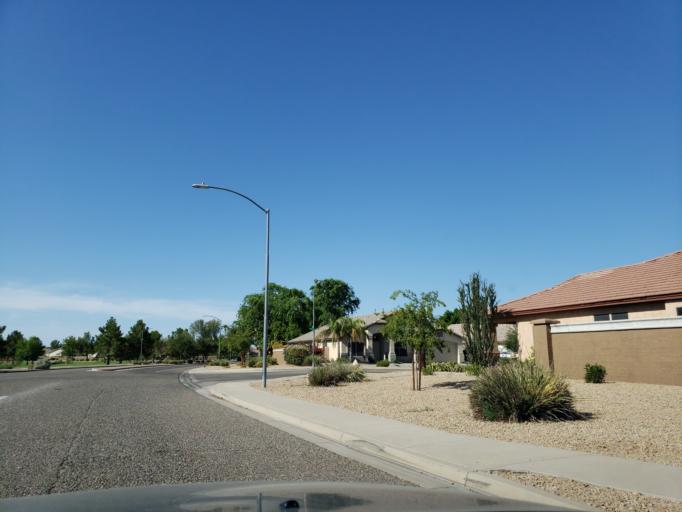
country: US
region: Arizona
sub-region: Maricopa County
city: Peoria
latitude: 33.6627
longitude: -112.1953
